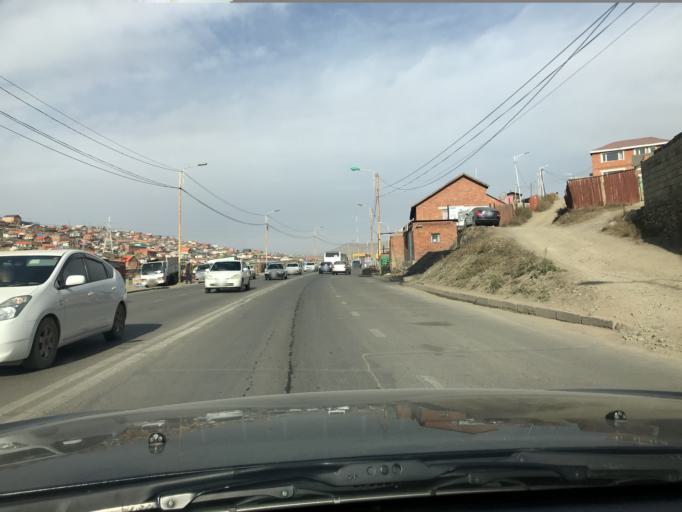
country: MN
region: Ulaanbaatar
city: Ulaanbaatar
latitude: 47.9351
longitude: 106.8850
